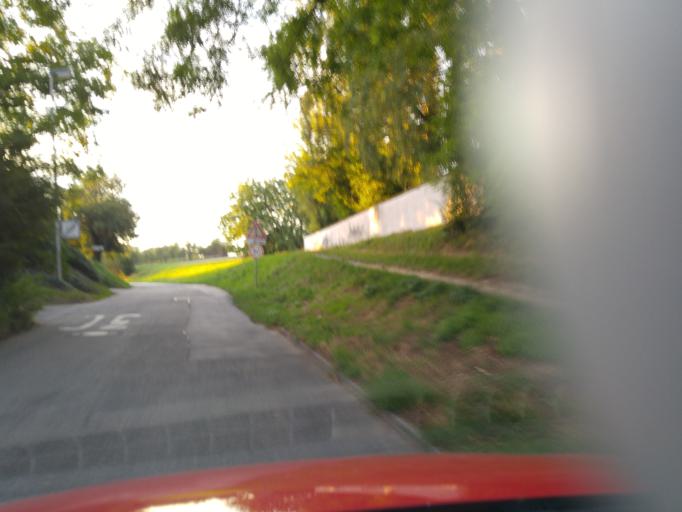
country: DE
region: Baden-Wuerttemberg
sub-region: Regierungsbezirk Stuttgart
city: Untereisesheim
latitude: 49.1990
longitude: 9.1964
